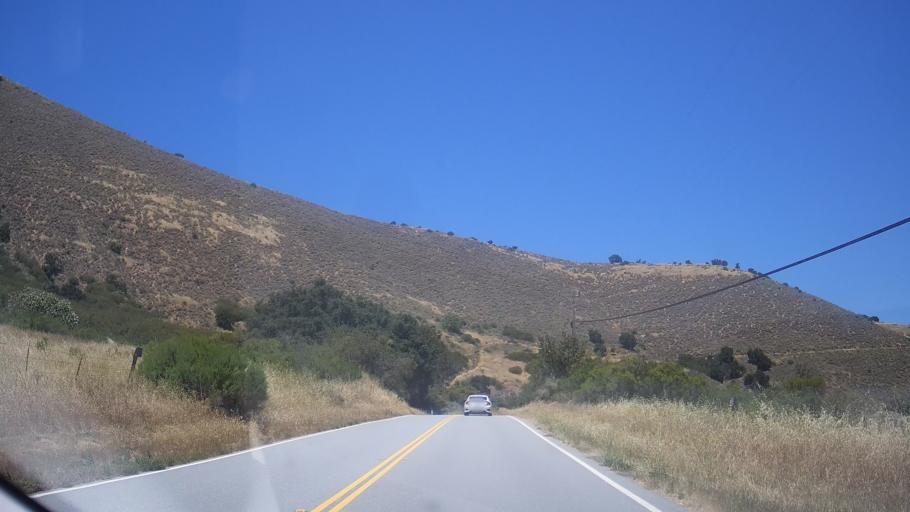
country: US
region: California
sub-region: Monterey County
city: Greenfield
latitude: 36.2407
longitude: -121.4444
